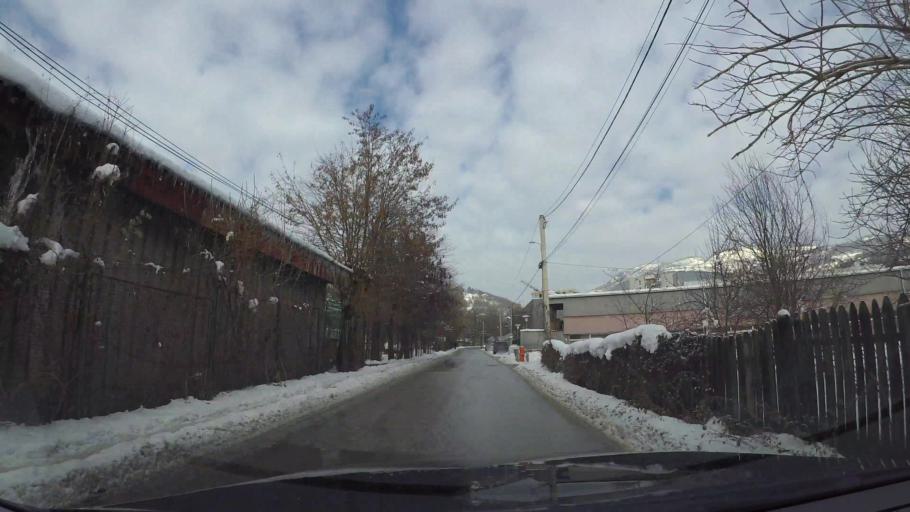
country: BA
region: Federation of Bosnia and Herzegovina
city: Kobilja Glava
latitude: 43.8788
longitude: 18.4138
